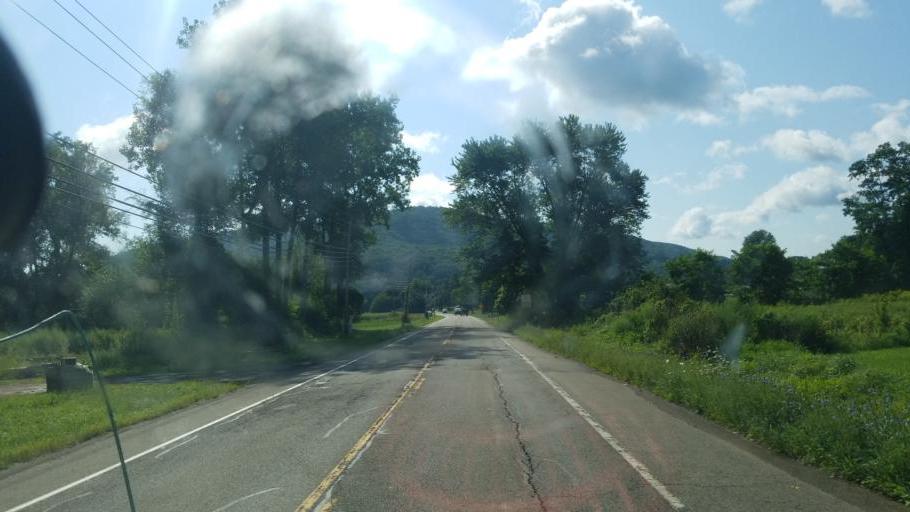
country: US
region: New York
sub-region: Steuben County
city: Canisteo
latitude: 42.2635
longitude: -77.5919
